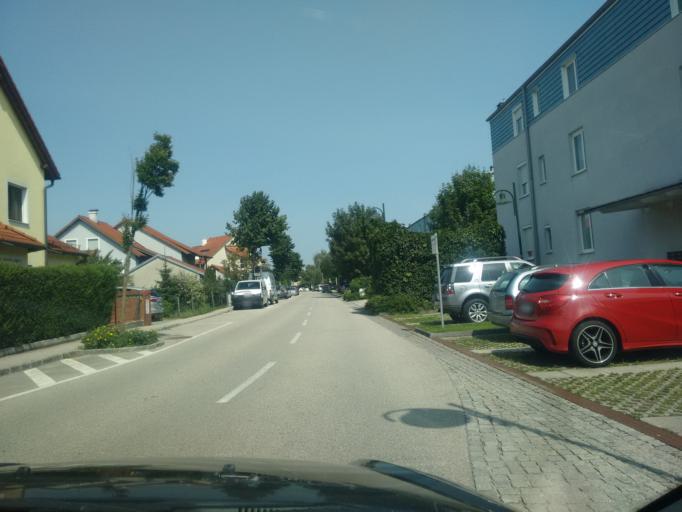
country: AT
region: Upper Austria
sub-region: Wels-Land
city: Gunskirchen
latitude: 48.1217
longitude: 13.9404
